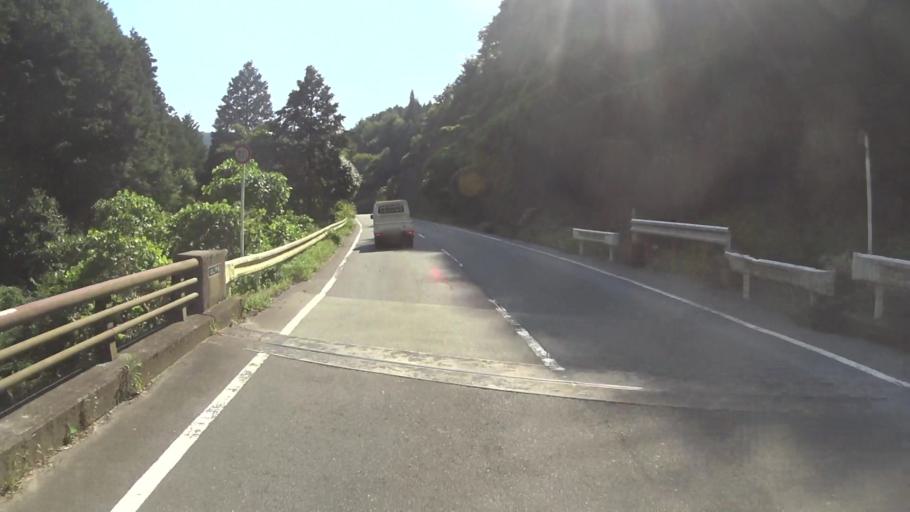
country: JP
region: Kyoto
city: Kameoka
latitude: 34.9723
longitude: 135.5716
